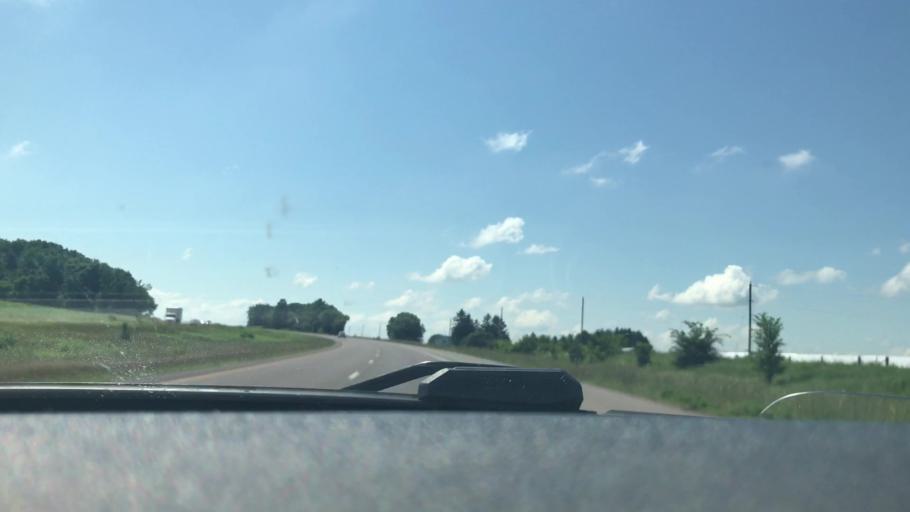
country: US
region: Wisconsin
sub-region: Chippewa County
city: Bloomer
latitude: 45.0485
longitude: -91.4654
